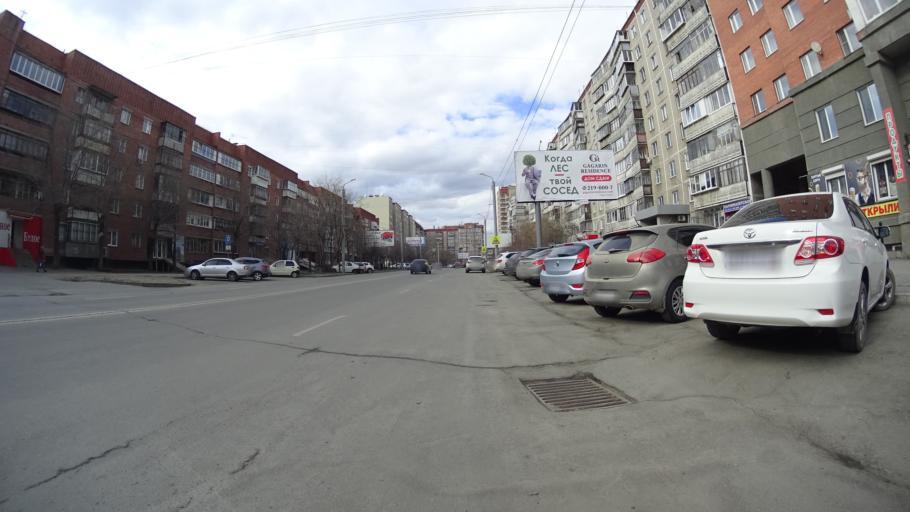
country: RU
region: Chelyabinsk
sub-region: Gorod Chelyabinsk
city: Chelyabinsk
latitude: 55.1509
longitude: 61.3806
